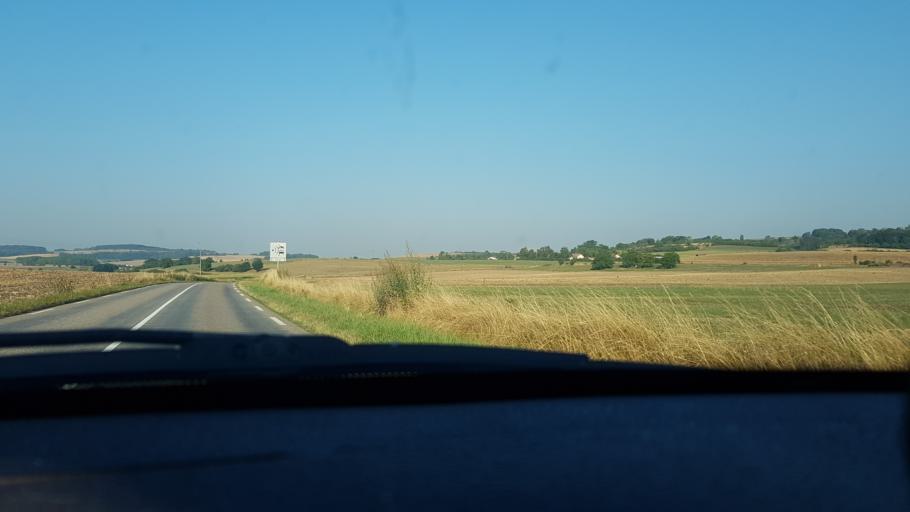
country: FR
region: Lorraine
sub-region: Departement des Vosges
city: Charmes
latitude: 48.3677
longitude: 6.2741
